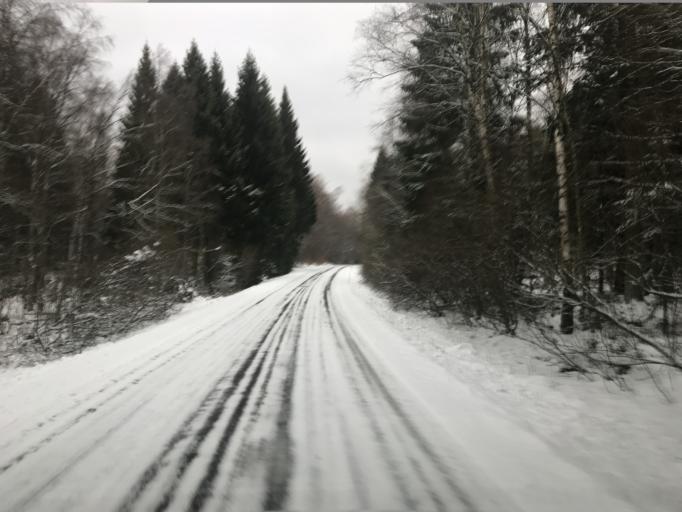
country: SE
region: Skane
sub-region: Kristianstads Kommun
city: Degeberga
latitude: 55.7865
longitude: 13.9439
